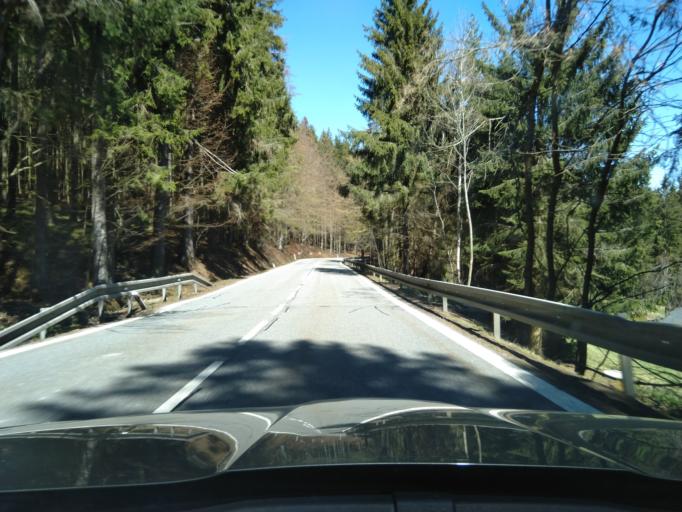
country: CZ
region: Jihocesky
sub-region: Okres Prachatice
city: Vimperk
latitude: 48.9962
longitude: 13.7679
